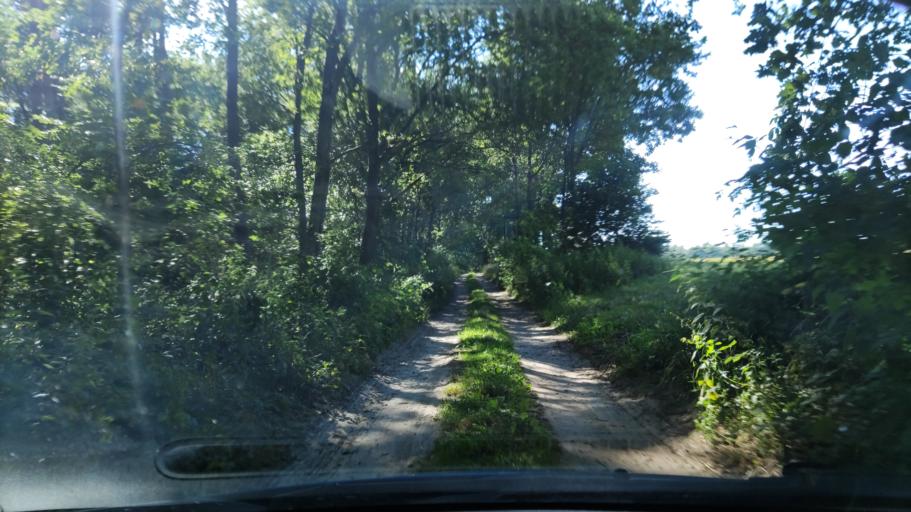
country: DE
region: Lower Saxony
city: Thomasburg
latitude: 53.1782
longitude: 10.6791
